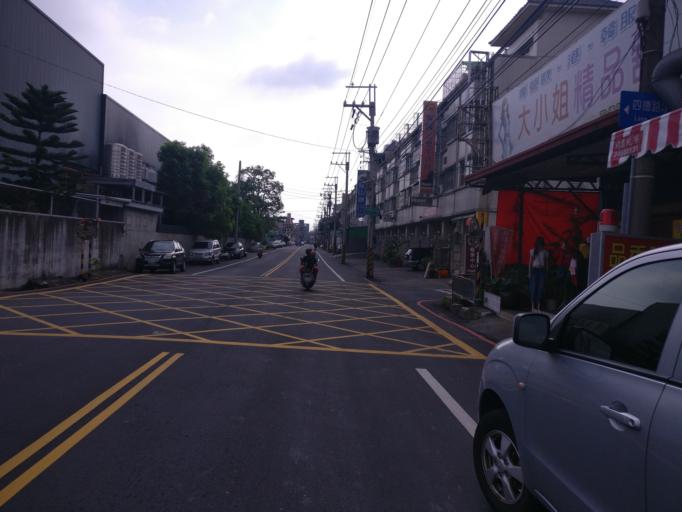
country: TW
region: Taiwan
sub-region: Taichung City
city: Taichung
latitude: 24.0656
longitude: 120.6851
